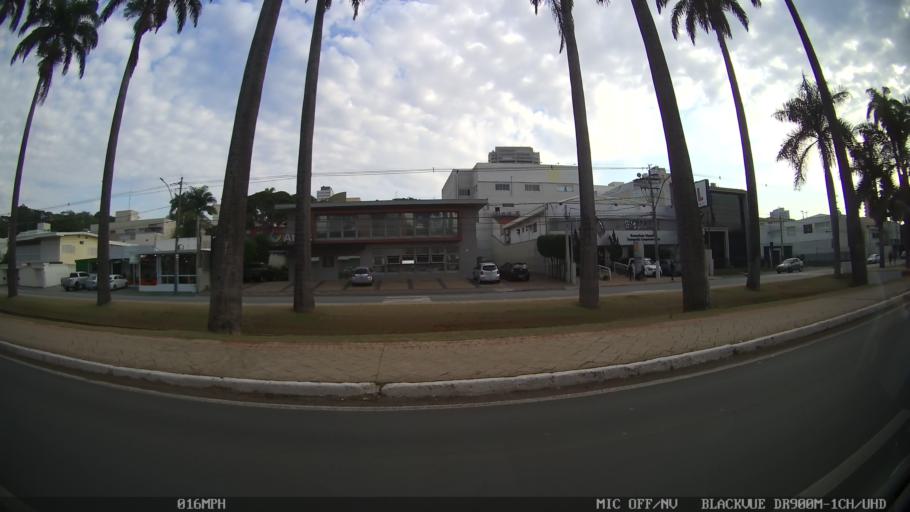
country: BR
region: Sao Paulo
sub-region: Americana
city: Americana
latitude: -22.7457
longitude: -47.3338
